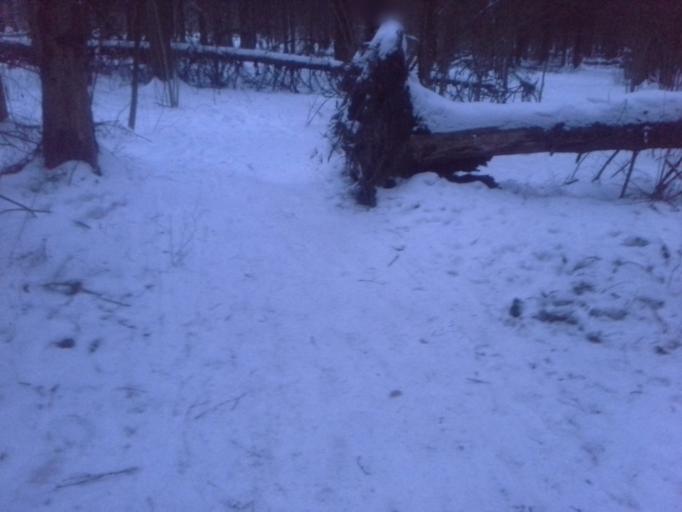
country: RU
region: Moscow
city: Yasenevo
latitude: 55.5647
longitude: 37.5476
